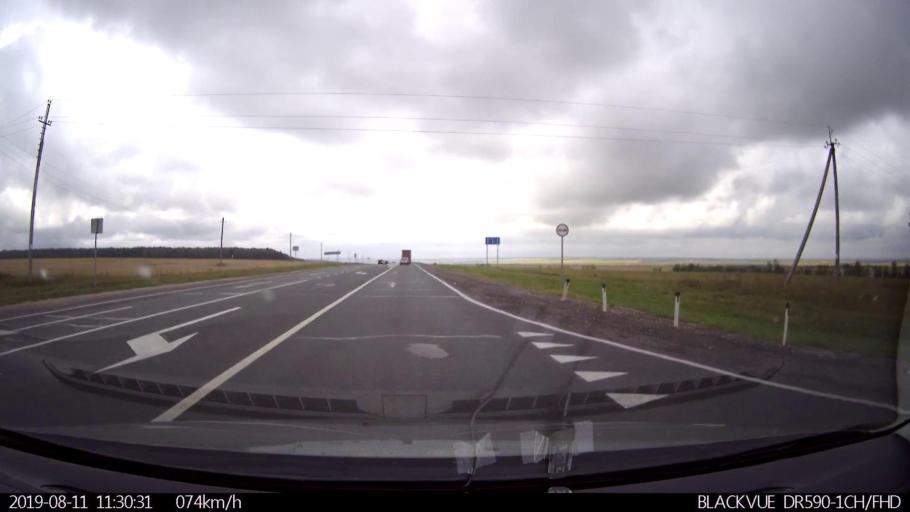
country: RU
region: Ulyanovsk
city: Krasnyy Gulyay
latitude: 54.0576
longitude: 48.2189
